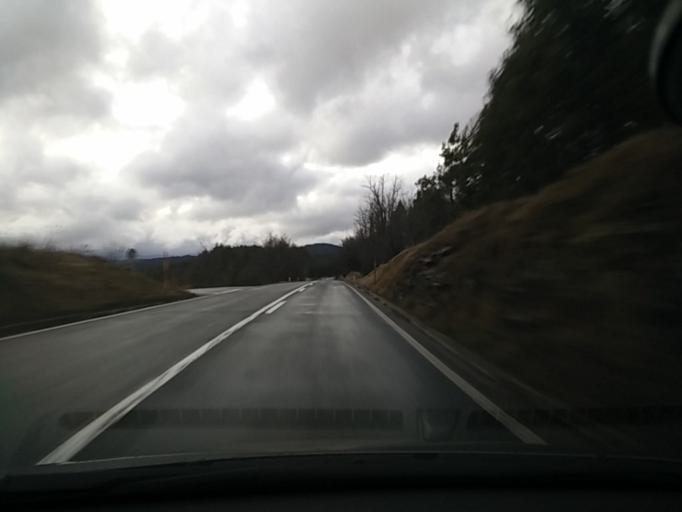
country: SI
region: Pivka
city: Pivka
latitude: 45.5247
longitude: 14.1354
